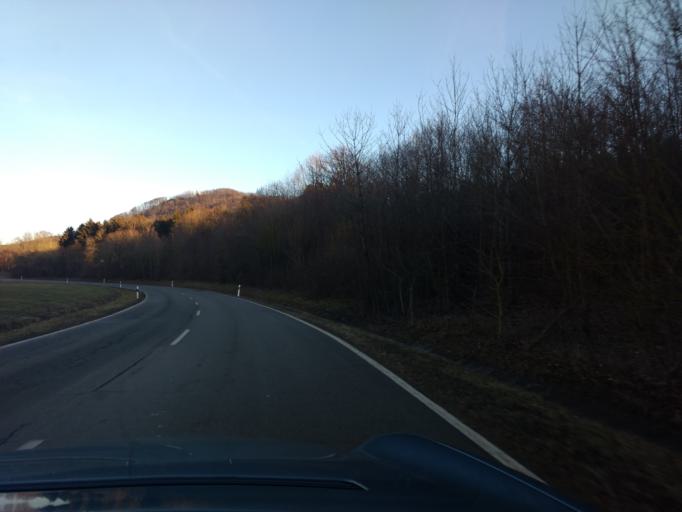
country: DE
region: Baden-Wuerttemberg
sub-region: Regierungsbezirk Stuttgart
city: Ottenbach
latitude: 48.7610
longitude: 9.7669
